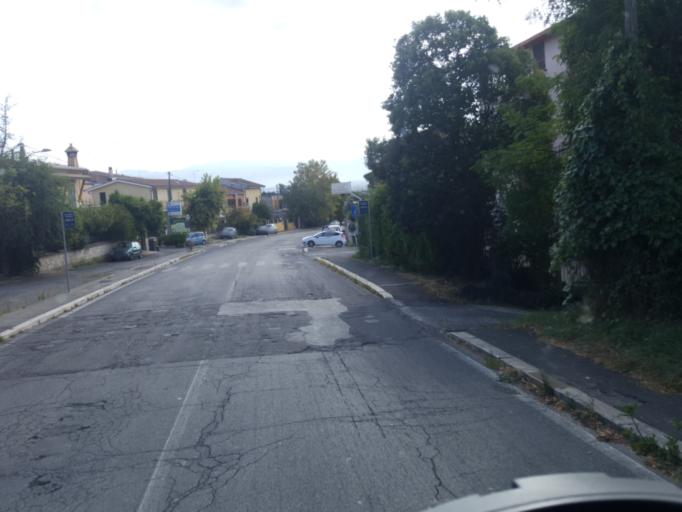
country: IT
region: Latium
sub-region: Citta metropolitana di Roma Capitale
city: Bivio di Capanelle
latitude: 42.1230
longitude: 12.5870
